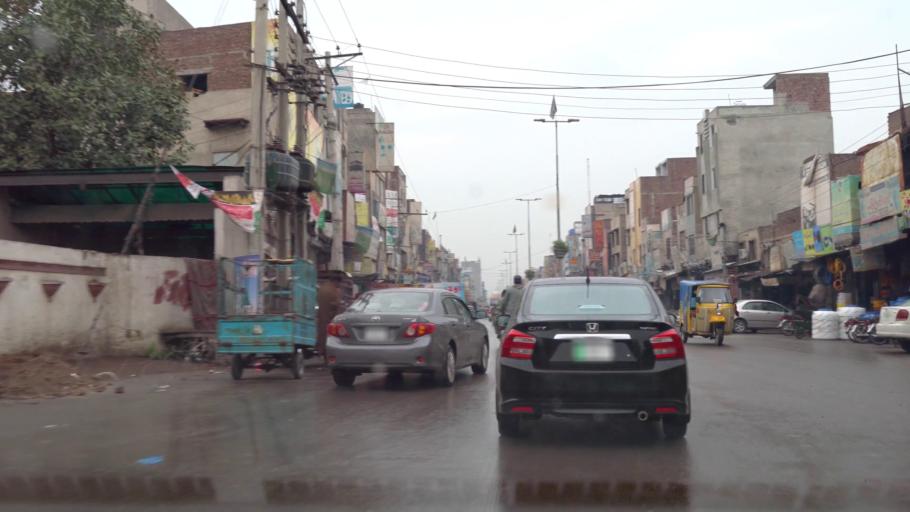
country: PK
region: Punjab
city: Faisalabad
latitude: 31.4136
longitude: 73.0909
